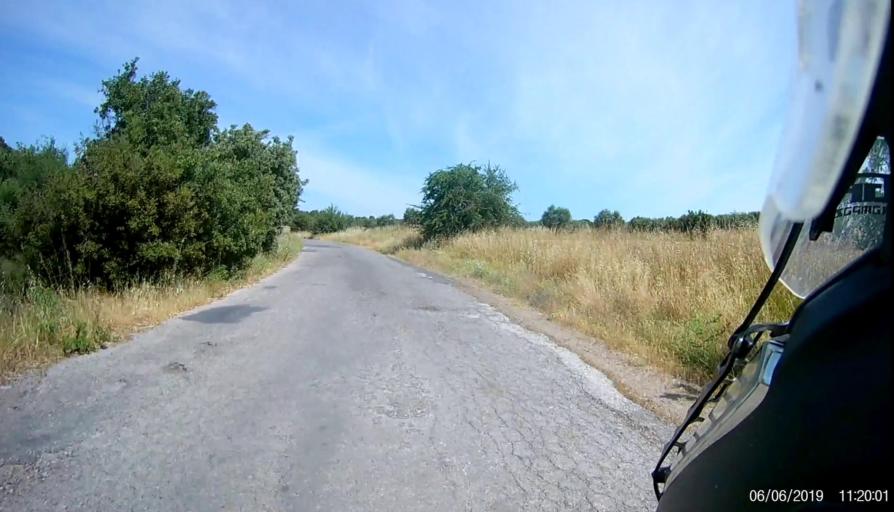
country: TR
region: Canakkale
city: Gulpinar
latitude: 39.6622
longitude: 26.1639
